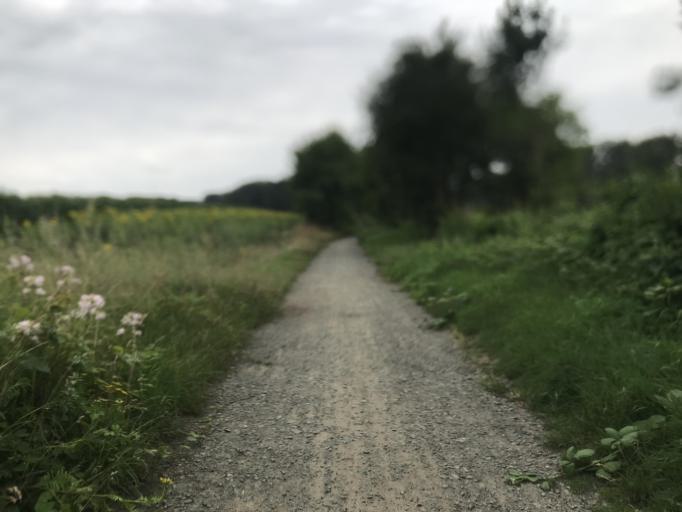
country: DE
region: Saxony-Anhalt
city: Quedlinburg
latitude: 51.7737
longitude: 11.1197
